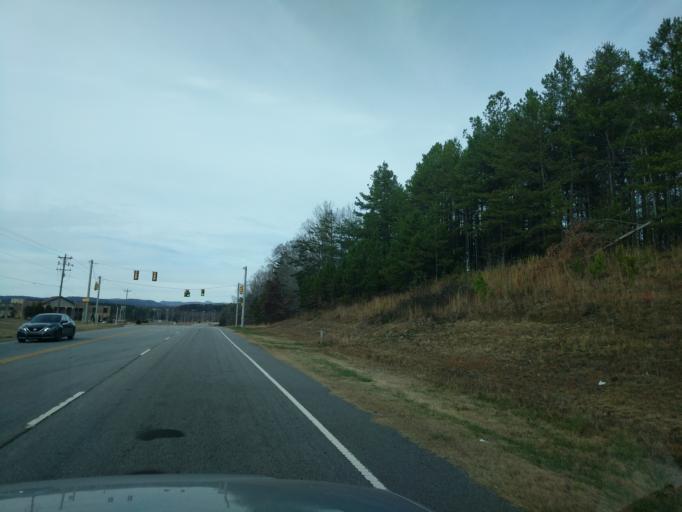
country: US
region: South Carolina
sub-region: Oconee County
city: Walhalla
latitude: 34.8138
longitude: -83.0366
